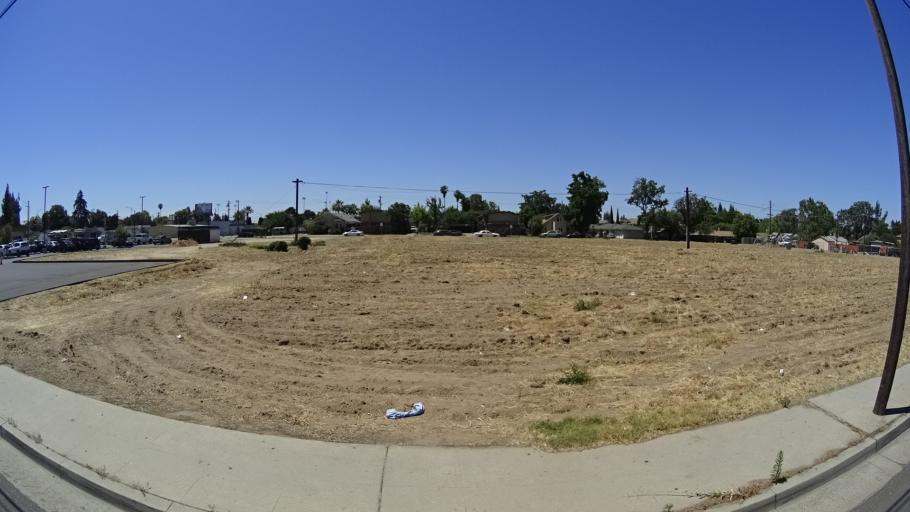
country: US
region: California
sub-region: Fresno County
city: Fresno
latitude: 36.7722
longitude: -119.7919
